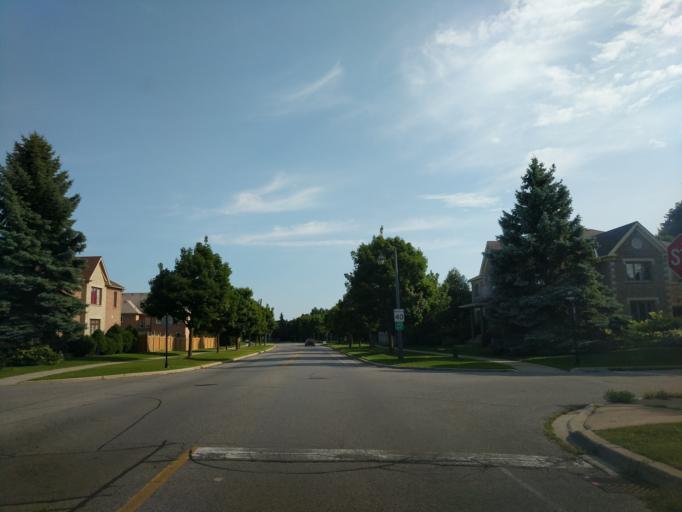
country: CA
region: Ontario
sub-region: York
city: Richmond Hill
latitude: 43.8673
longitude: -79.4007
